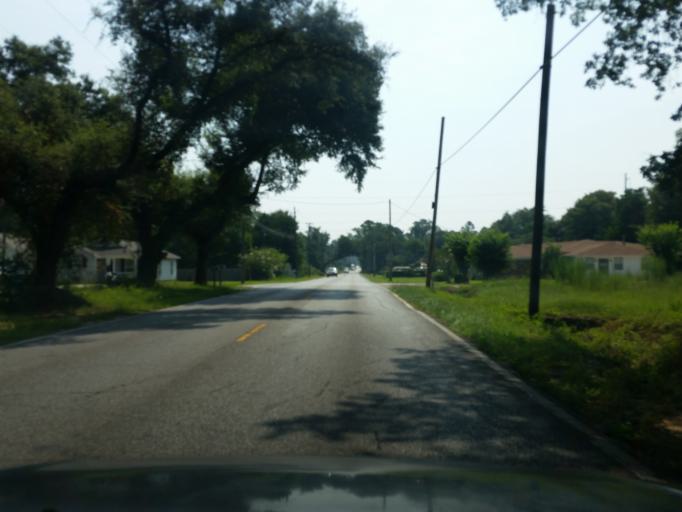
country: US
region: Florida
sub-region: Escambia County
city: Ensley
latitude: 30.5190
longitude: -87.2822
